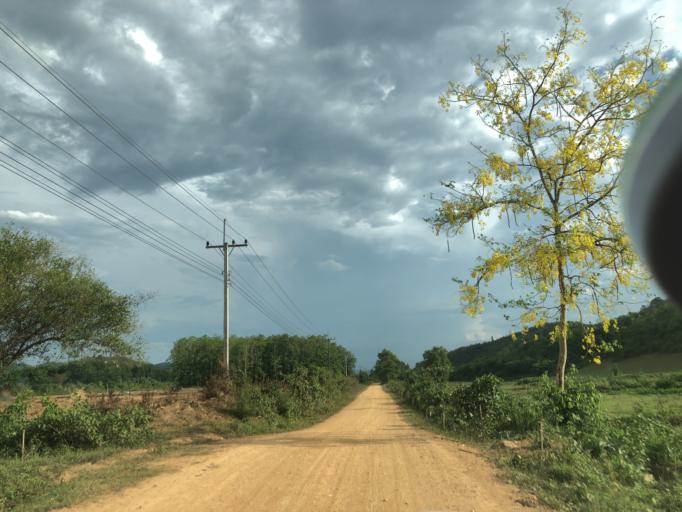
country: TH
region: Loei
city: Chiang Khan
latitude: 18.0044
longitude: 101.4204
